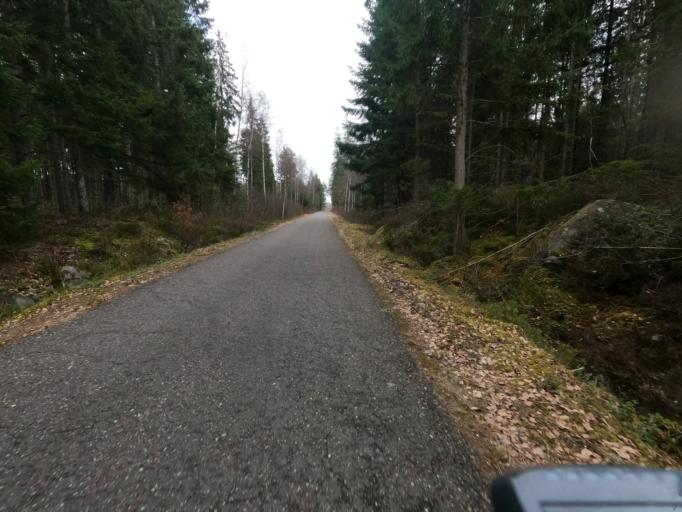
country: SE
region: Joenkoeping
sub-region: Varnamo Kommun
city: Rydaholm
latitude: 56.8455
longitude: 14.2173
